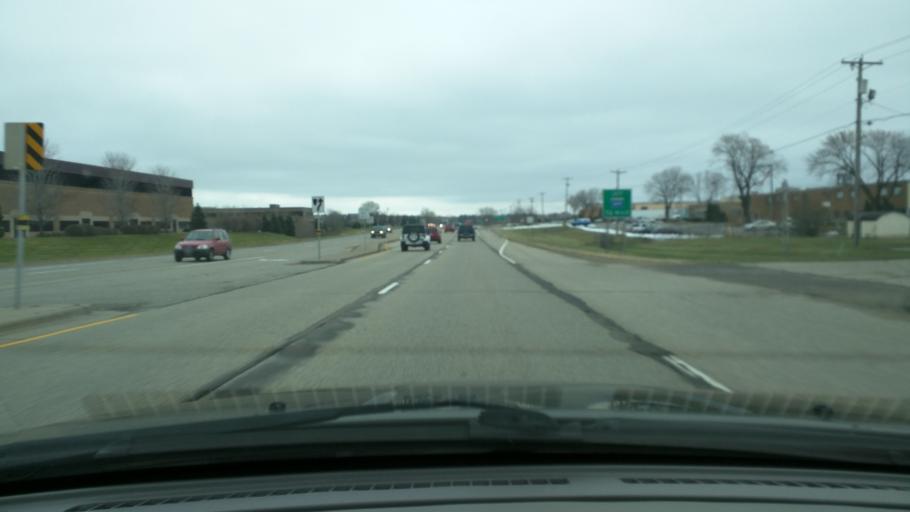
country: US
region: Minnesota
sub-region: Dakota County
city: Mendota Heights
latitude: 44.8571
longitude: -93.1415
